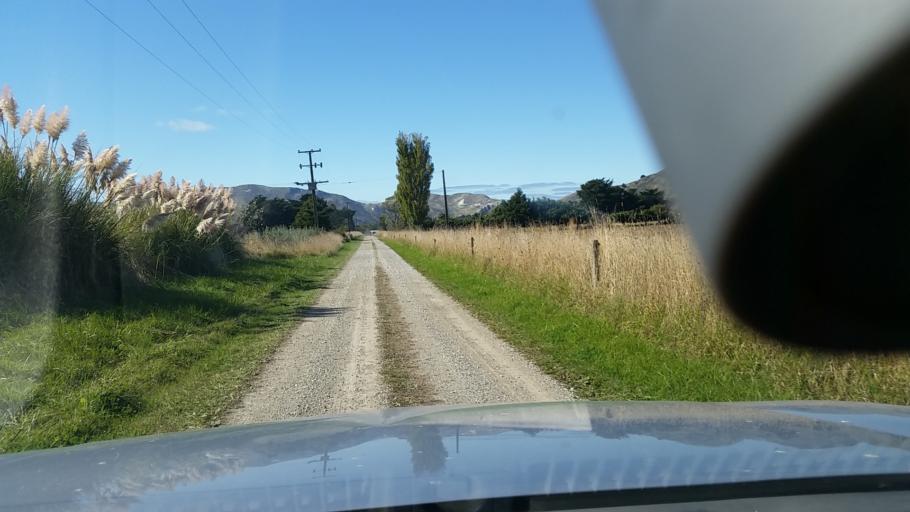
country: NZ
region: Marlborough
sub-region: Marlborough District
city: Blenheim
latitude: -41.8246
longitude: 174.1226
